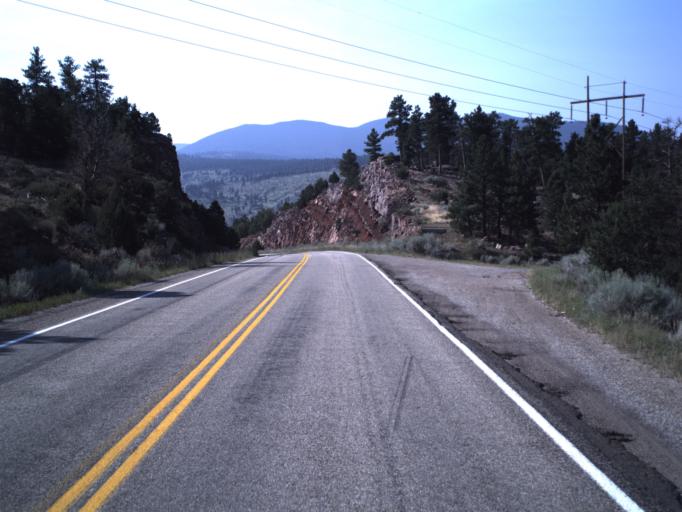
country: US
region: Utah
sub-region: Daggett County
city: Manila
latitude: 40.9176
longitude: -109.4150
